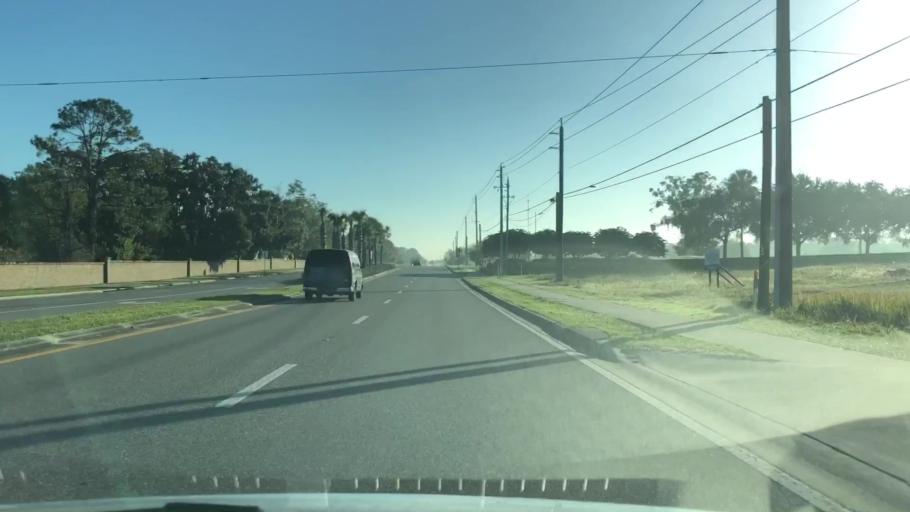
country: US
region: Florida
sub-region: Seminole County
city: Lake Mary
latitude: 28.7864
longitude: -81.3231
